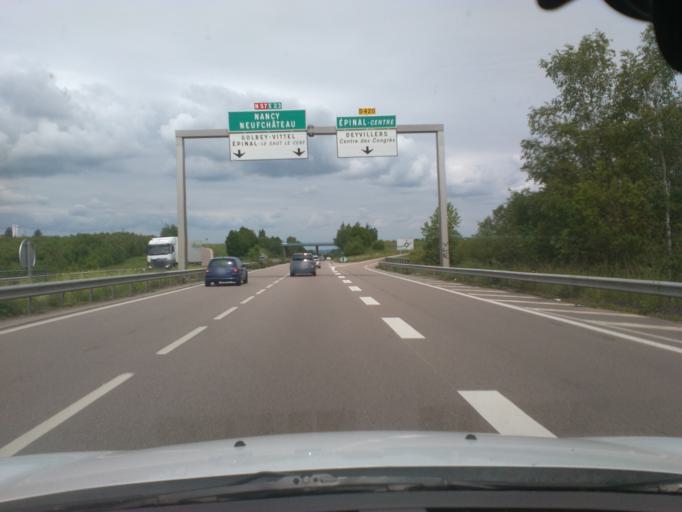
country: FR
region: Lorraine
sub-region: Departement des Vosges
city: Epinal
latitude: 48.1861
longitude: 6.4816
